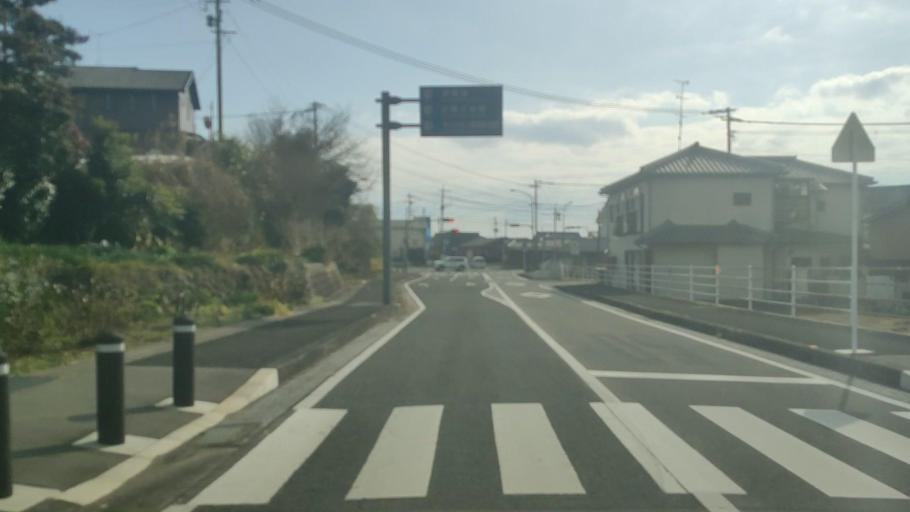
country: JP
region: Nagasaki
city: Shimabara
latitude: 32.6552
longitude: 130.2885
